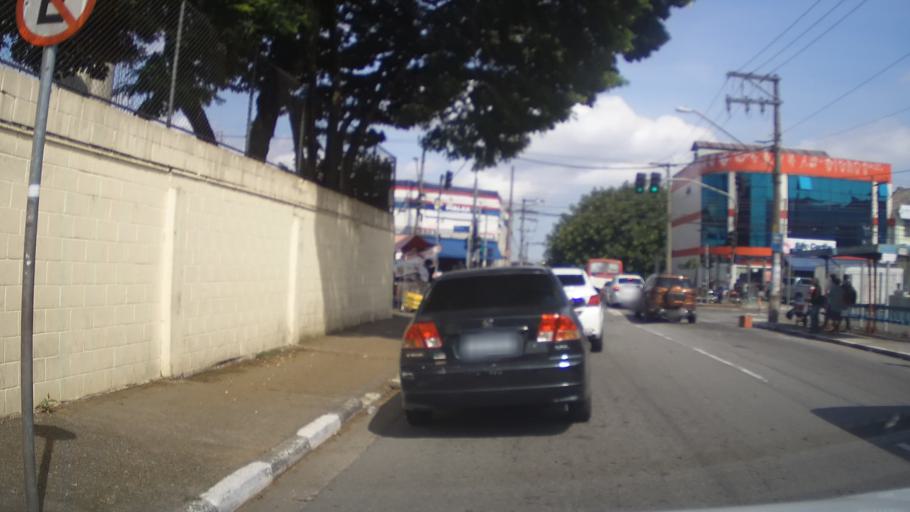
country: BR
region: Sao Paulo
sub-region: Guarulhos
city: Guarulhos
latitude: -23.4497
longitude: -46.4741
